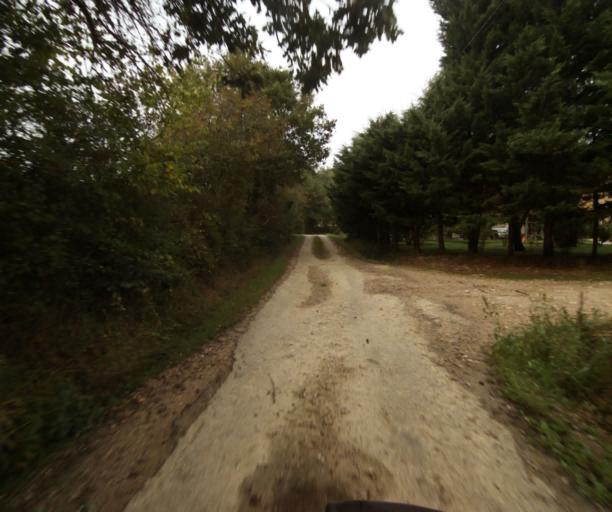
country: FR
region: Midi-Pyrenees
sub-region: Departement du Tarn-et-Garonne
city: Saint-Nauphary
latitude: 43.9414
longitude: 1.4425
